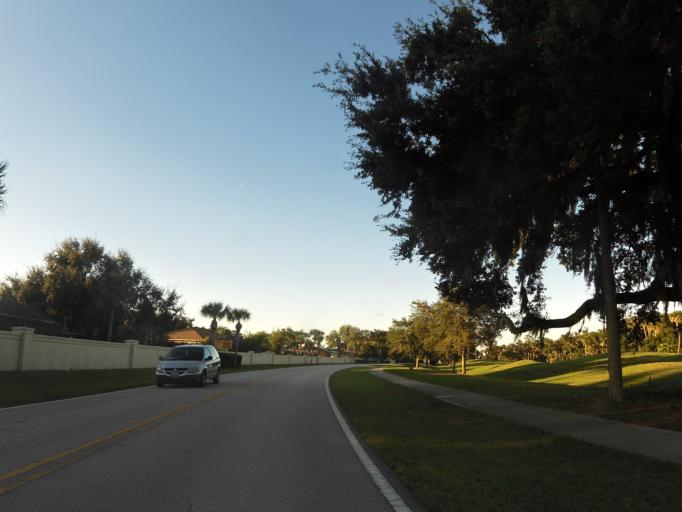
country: US
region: Florida
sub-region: Flagler County
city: Palm Coast
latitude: 29.5616
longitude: -81.2041
